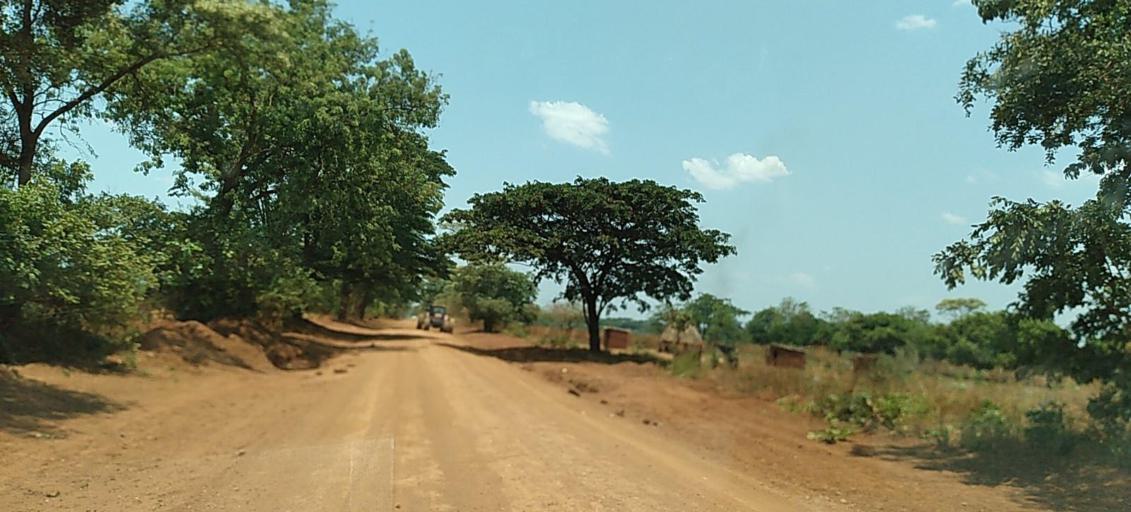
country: ZM
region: Copperbelt
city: Mpongwe
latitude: -13.5152
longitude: 28.0136
